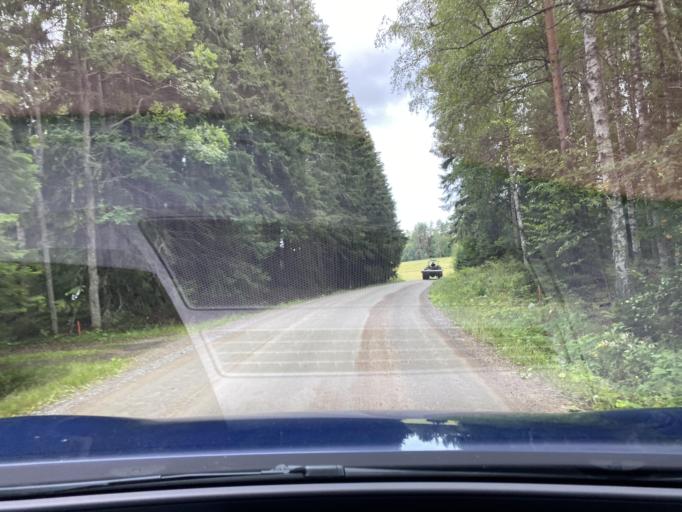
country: FI
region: Pirkanmaa
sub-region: Lounais-Pirkanmaa
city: Punkalaidun
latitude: 61.1746
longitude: 23.1809
